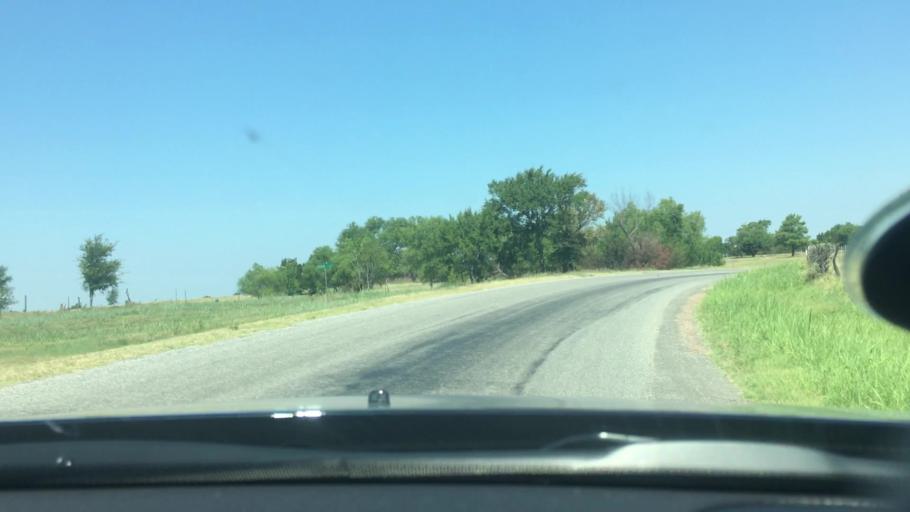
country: US
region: Oklahoma
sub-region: Johnston County
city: Tishomingo
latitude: 34.3105
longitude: -96.6354
